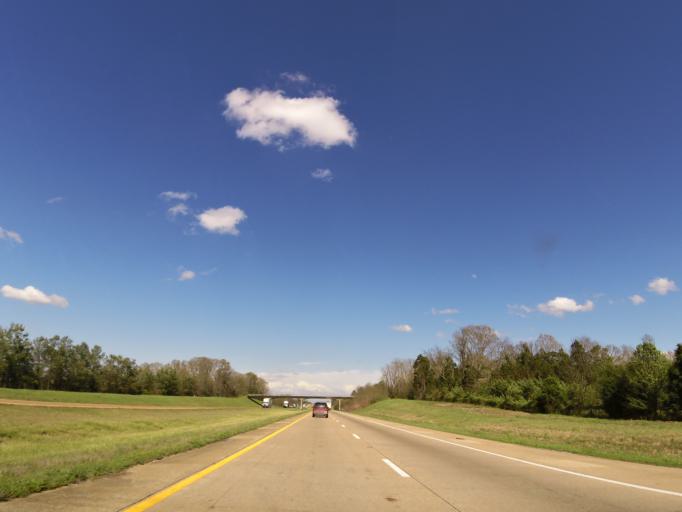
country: US
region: Tennessee
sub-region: Gibson County
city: Medina
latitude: 35.6937
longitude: -88.7031
